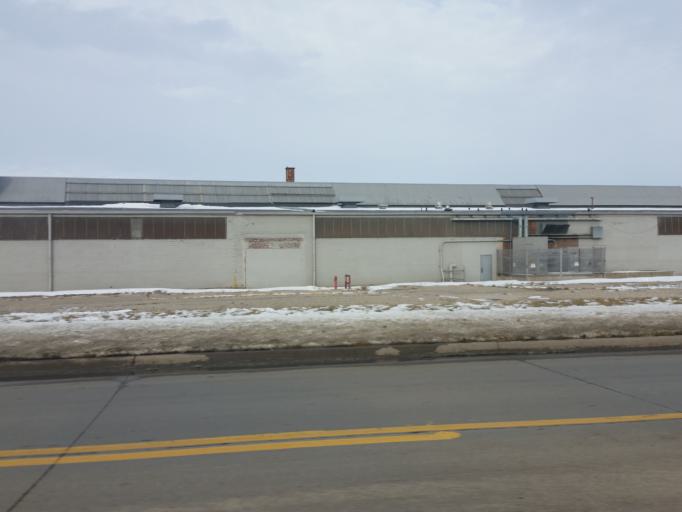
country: US
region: Iowa
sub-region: Black Hawk County
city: Waterloo
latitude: 42.5006
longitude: -92.3491
